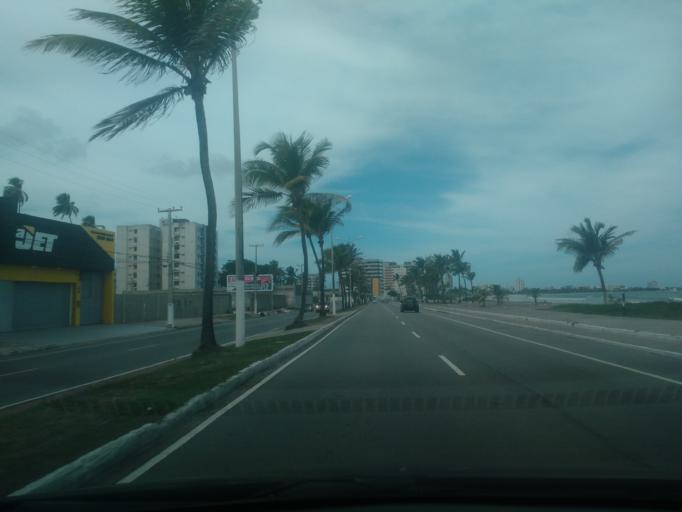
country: BR
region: Alagoas
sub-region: Maceio
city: Maceio
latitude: -9.6717
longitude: -35.7445
